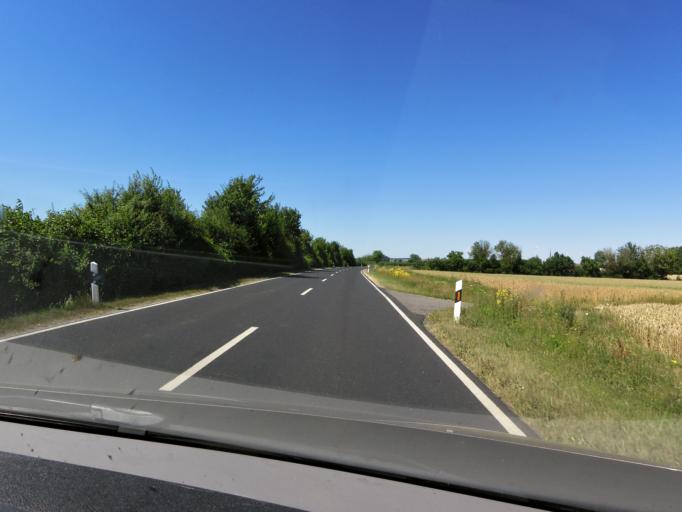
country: DE
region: Bavaria
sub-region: Regierungsbezirk Unterfranken
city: Biebelried
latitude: 49.7205
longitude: 10.0829
